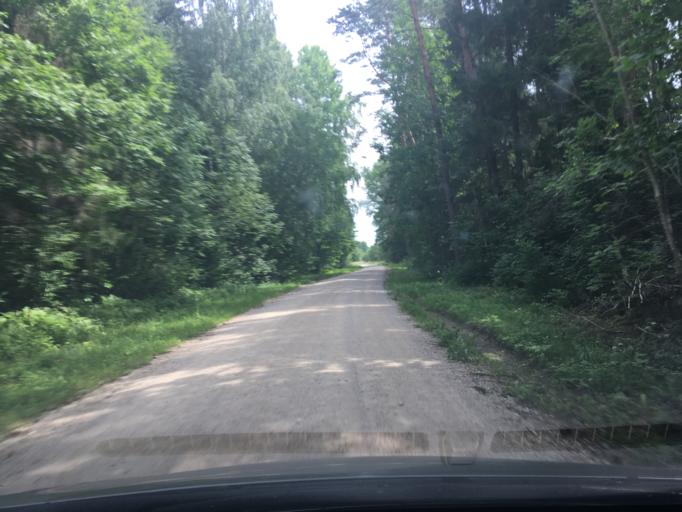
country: EE
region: Raplamaa
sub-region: Maerjamaa vald
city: Marjamaa
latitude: 58.9471
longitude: 24.5588
